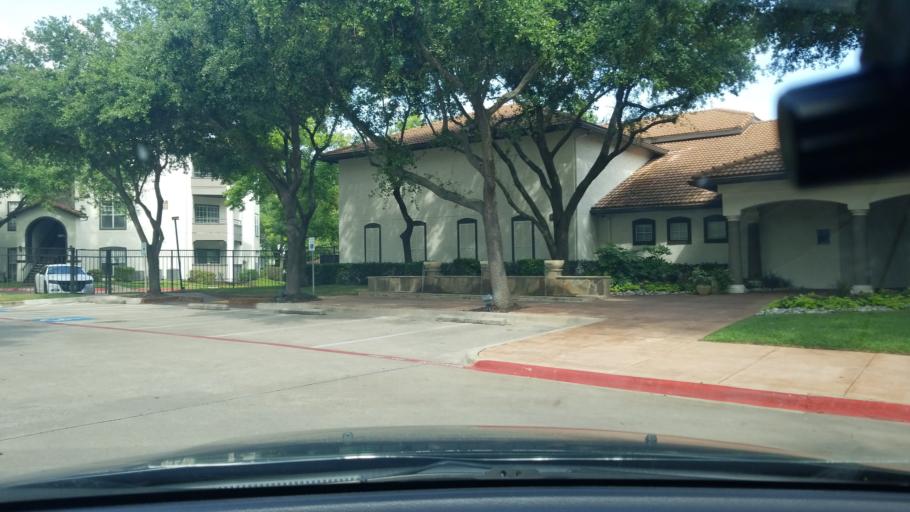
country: US
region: Texas
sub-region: Dallas County
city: Highland Park
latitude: 32.8304
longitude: -96.7086
